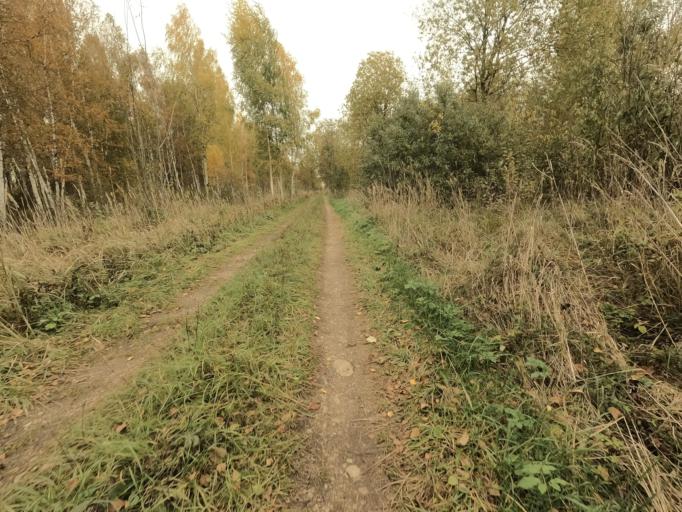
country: RU
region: Novgorod
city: Pankovka
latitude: 58.8770
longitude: 30.9408
